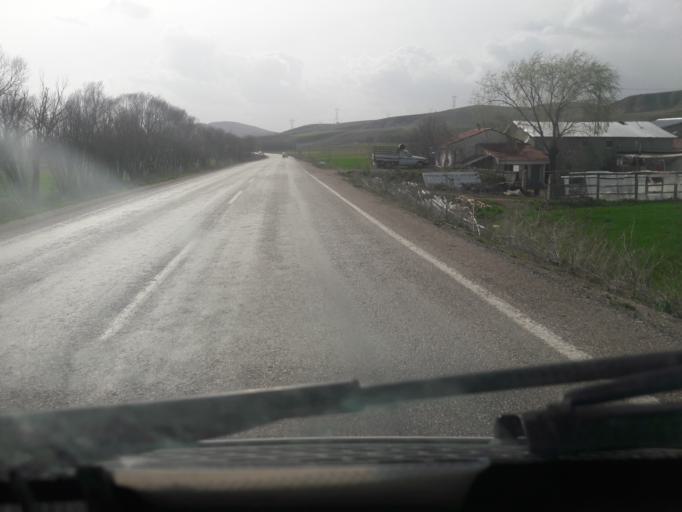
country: TR
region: Gumushane
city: Kelkit
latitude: 40.1430
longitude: 39.4180
